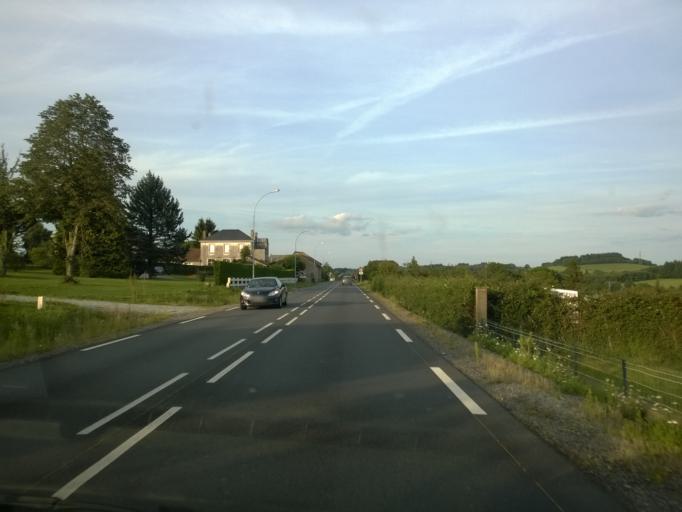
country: FR
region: Limousin
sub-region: Departement de la Haute-Vienne
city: Neuvic-Entier
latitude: 45.7300
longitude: 1.6632
